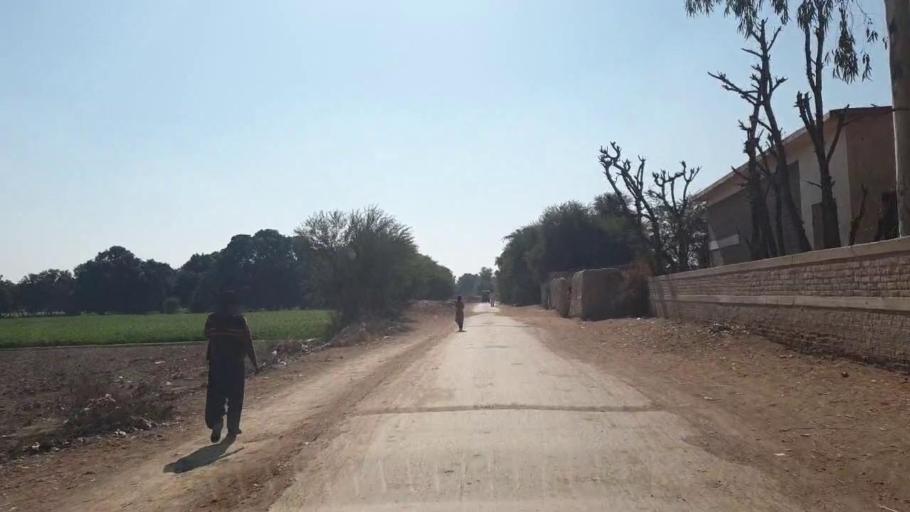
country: PK
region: Sindh
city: Shahpur Chakar
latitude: 26.1076
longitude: 68.6359
